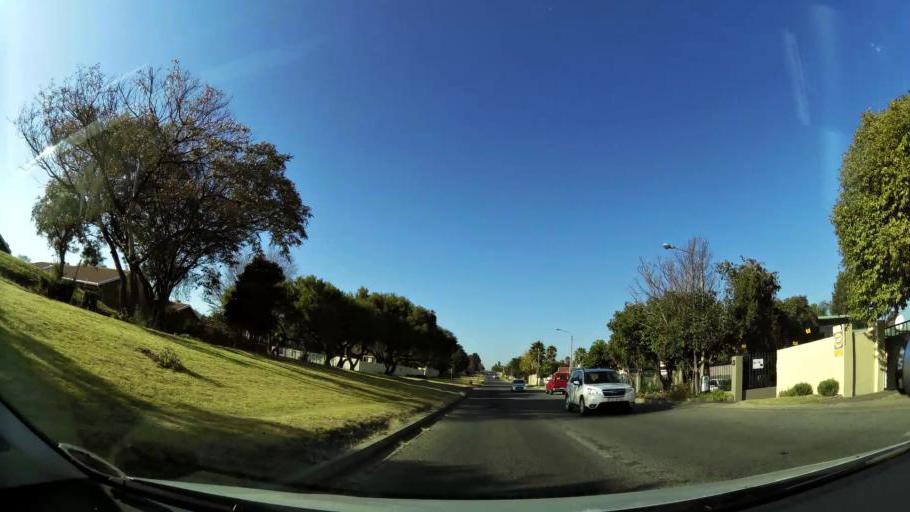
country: ZA
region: Gauteng
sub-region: City of Johannesburg Metropolitan Municipality
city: Modderfontein
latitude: -26.1330
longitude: 28.1657
